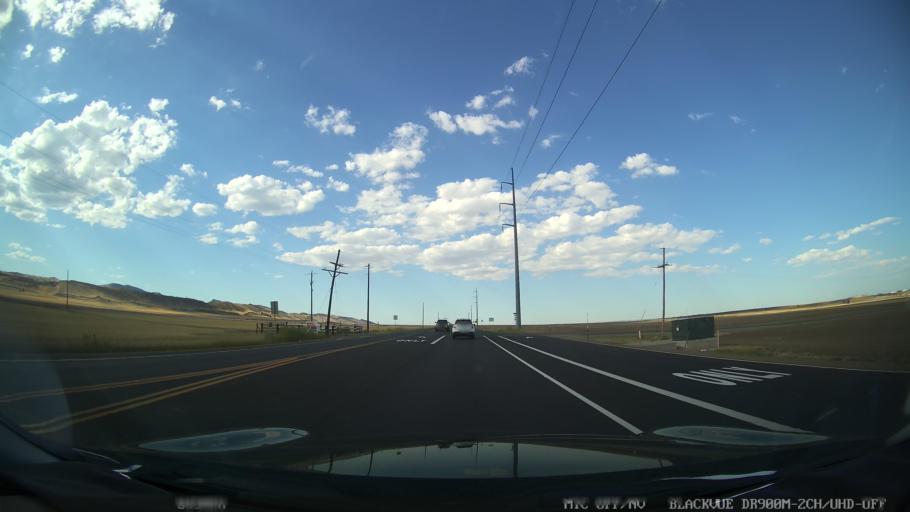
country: US
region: Colorado
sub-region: Larimer County
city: Loveland
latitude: 40.4497
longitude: -105.1155
